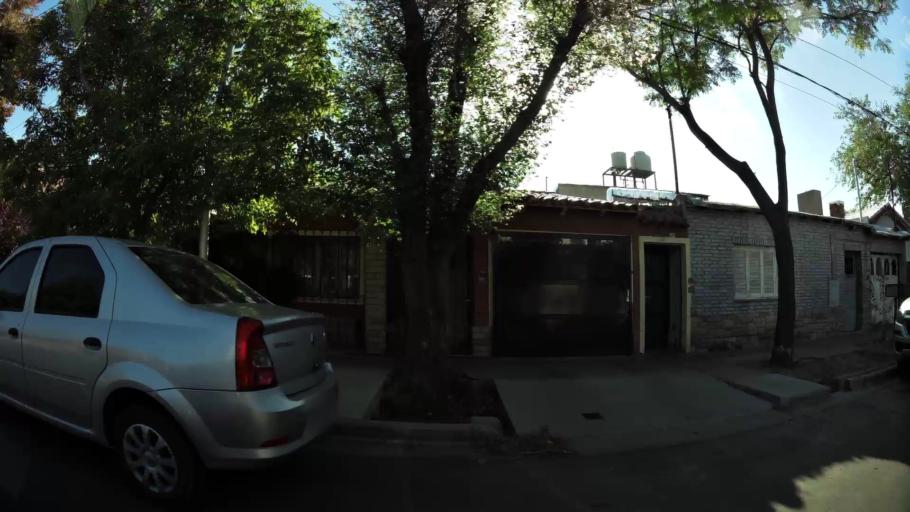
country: AR
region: Mendoza
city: Mendoza
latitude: -32.9015
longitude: -68.8352
